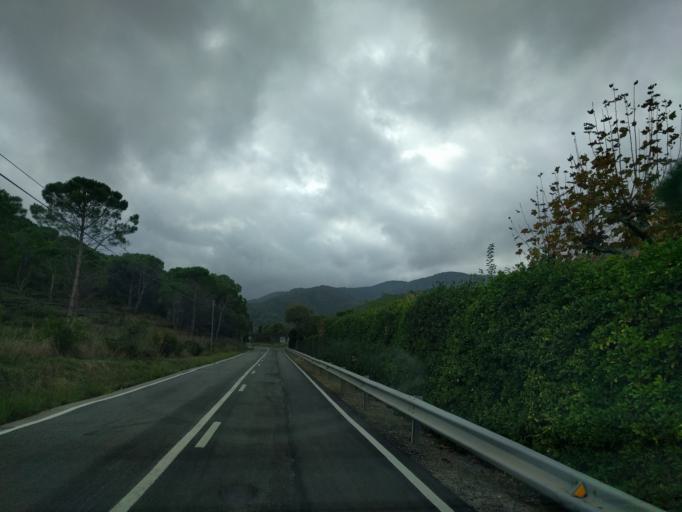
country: ES
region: Catalonia
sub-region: Provincia de Girona
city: Llanca
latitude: 42.3263
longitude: 3.2053
